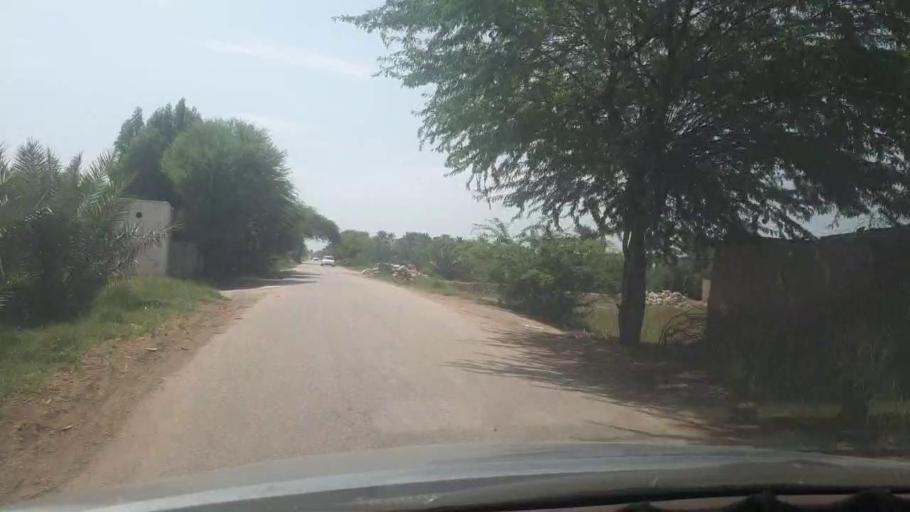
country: PK
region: Sindh
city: Bozdar
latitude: 27.2080
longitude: 68.5784
